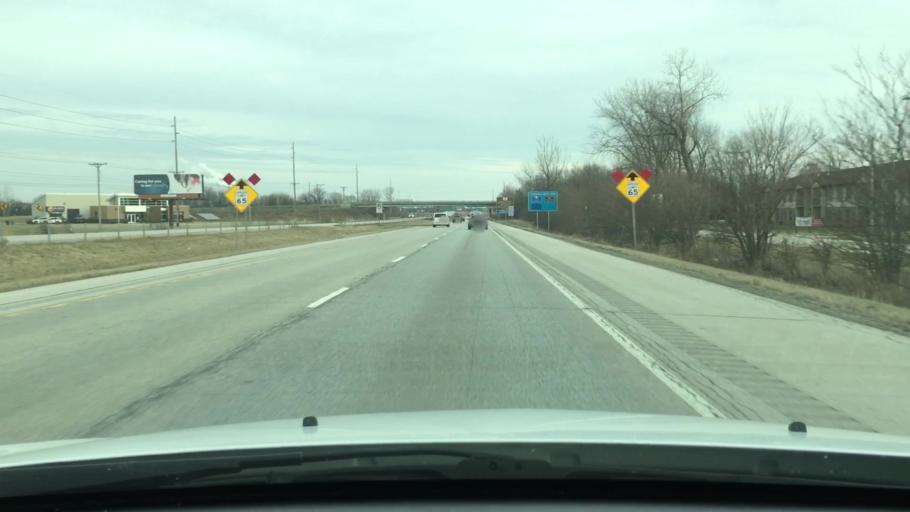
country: US
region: Illinois
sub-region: Sangamon County
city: Southern View
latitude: 39.7425
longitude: -89.6576
